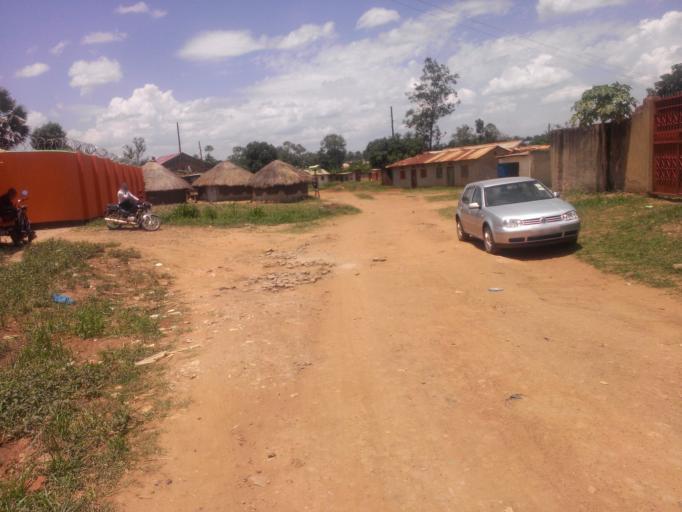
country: UG
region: Northern Region
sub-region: Gulu District
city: Gulu
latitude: 2.7817
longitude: 32.2935
